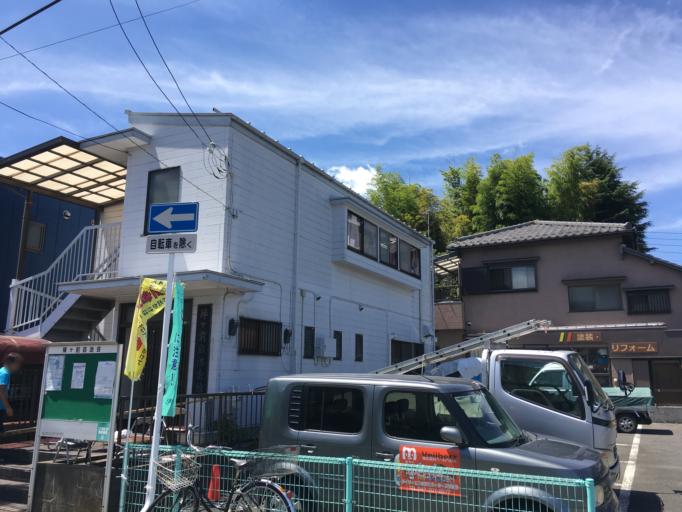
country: JP
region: Chiba
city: Matsudo
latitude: 35.7740
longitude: 139.9075
